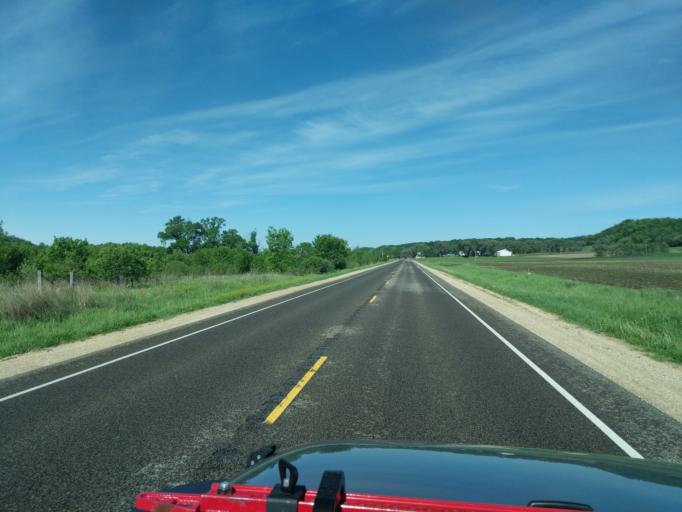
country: US
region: Wisconsin
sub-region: Pierce County
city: River Falls
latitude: 44.8510
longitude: -92.5673
